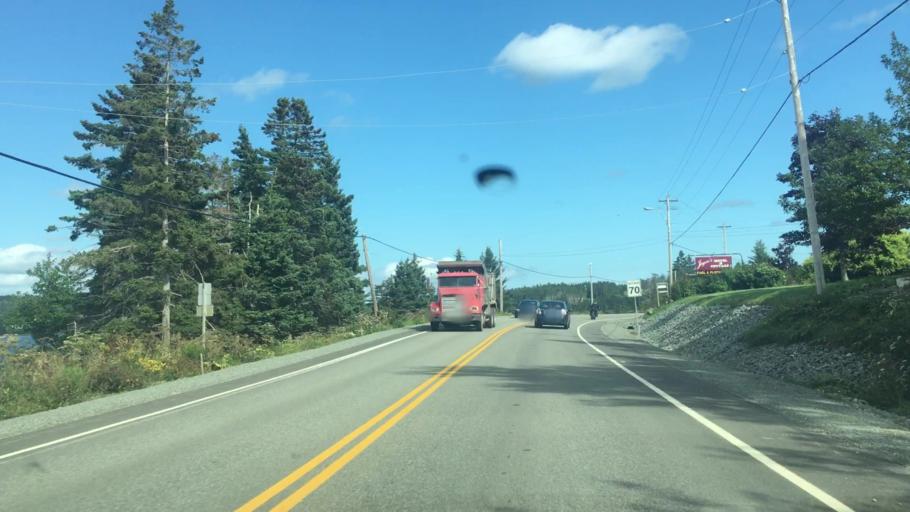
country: CA
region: Nova Scotia
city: Princeville
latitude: 45.6513
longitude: -60.8552
